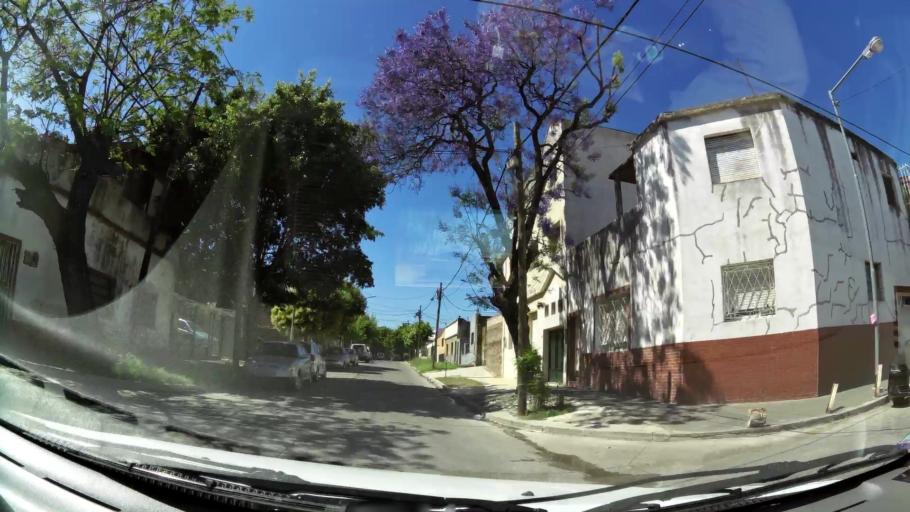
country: AR
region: Buenos Aires
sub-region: Partido de General San Martin
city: General San Martin
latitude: -34.5837
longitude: -58.5270
